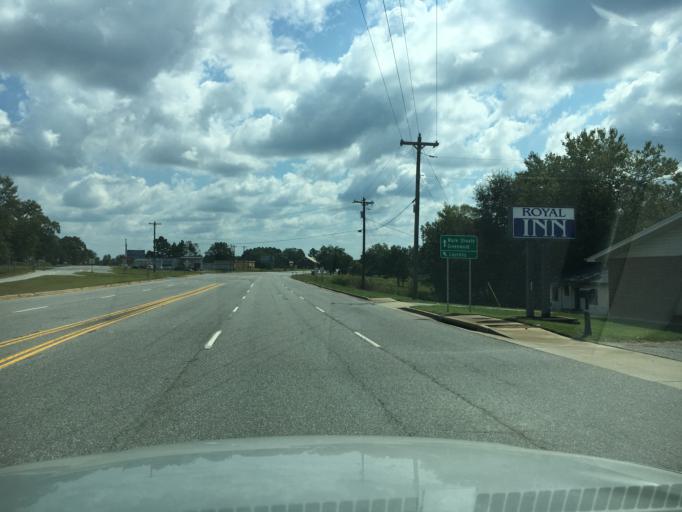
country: US
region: South Carolina
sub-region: Greenwood County
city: Ware Shoals
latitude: 34.5015
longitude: -82.2908
